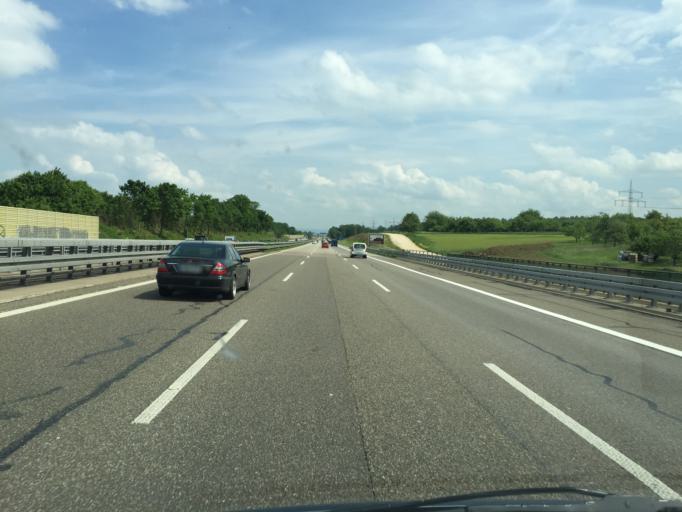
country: DE
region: Baden-Wuerttemberg
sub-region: Regierungsbezirk Stuttgart
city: Denkendorf
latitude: 48.6891
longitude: 9.3141
